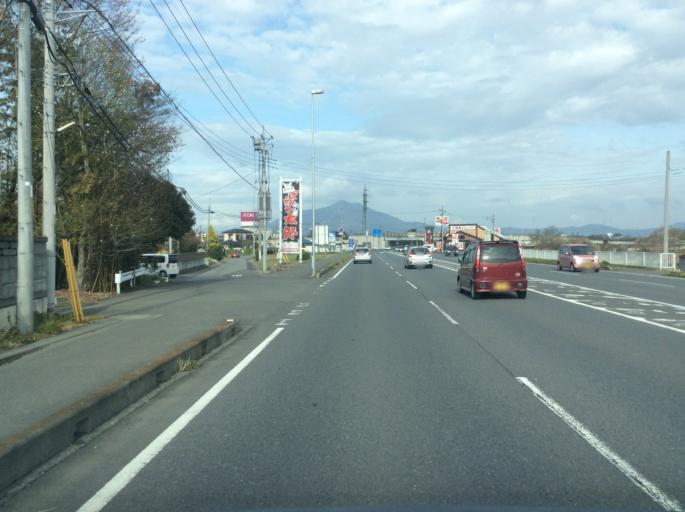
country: JP
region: Ibaraki
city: Ishige
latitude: 36.1871
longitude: 139.9847
